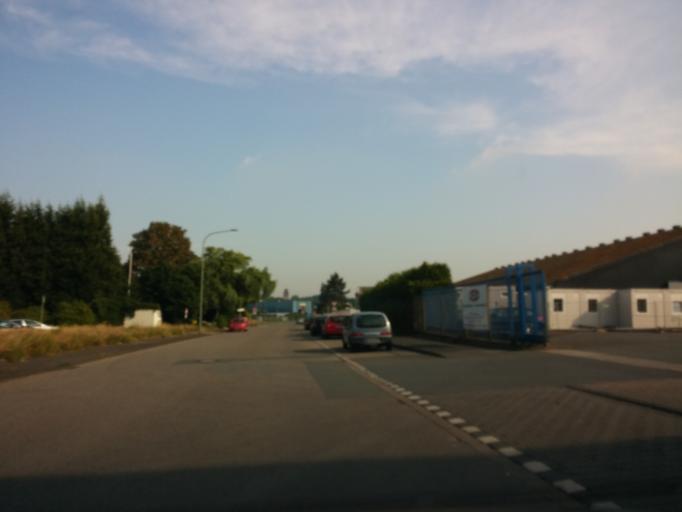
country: DE
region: North Rhine-Westphalia
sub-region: Regierungsbezirk Munster
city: Bottrop
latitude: 51.5132
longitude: 6.9533
